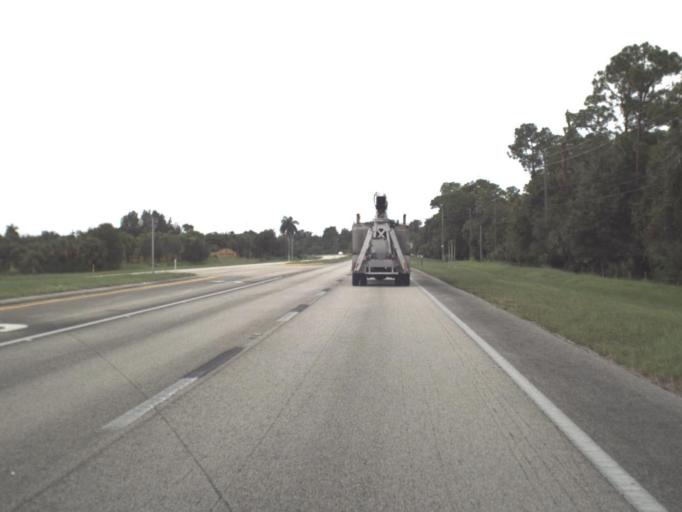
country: US
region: Florida
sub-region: Lee County
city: Olga
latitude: 26.7147
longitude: -81.6684
